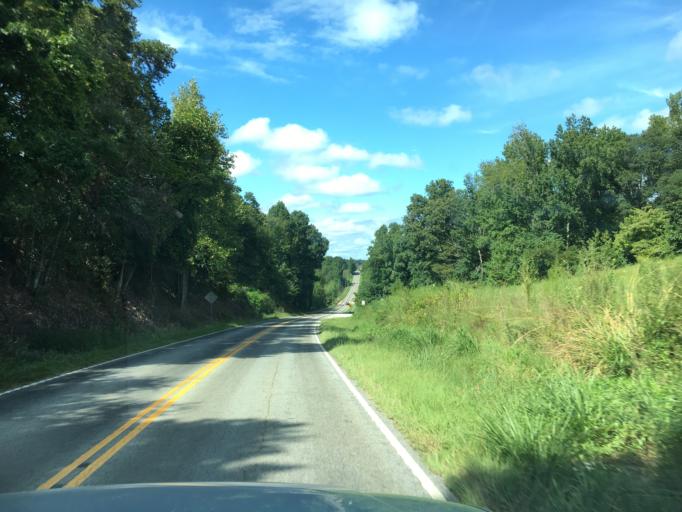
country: US
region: South Carolina
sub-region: Spartanburg County
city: Inman Mills
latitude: 35.0017
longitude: -82.1123
